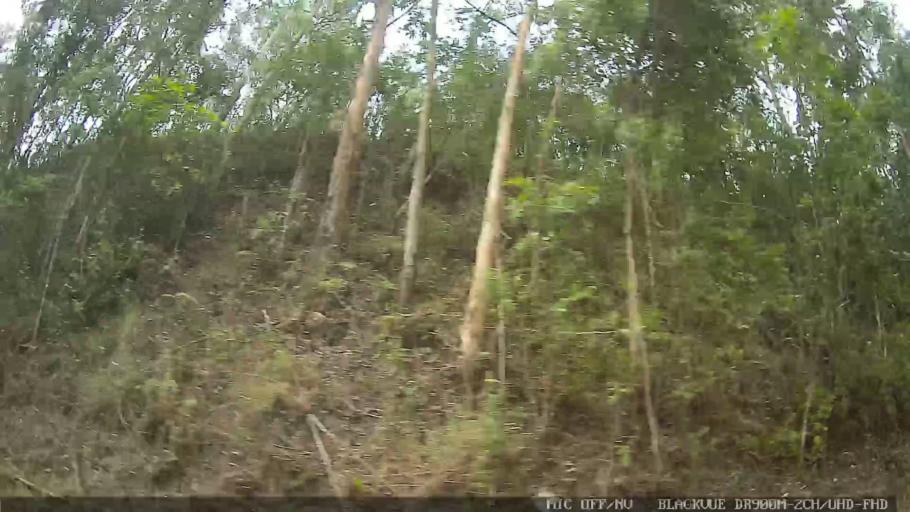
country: BR
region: Sao Paulo
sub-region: Itatiba
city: Itatiba
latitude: -22.8946
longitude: -46.7904
